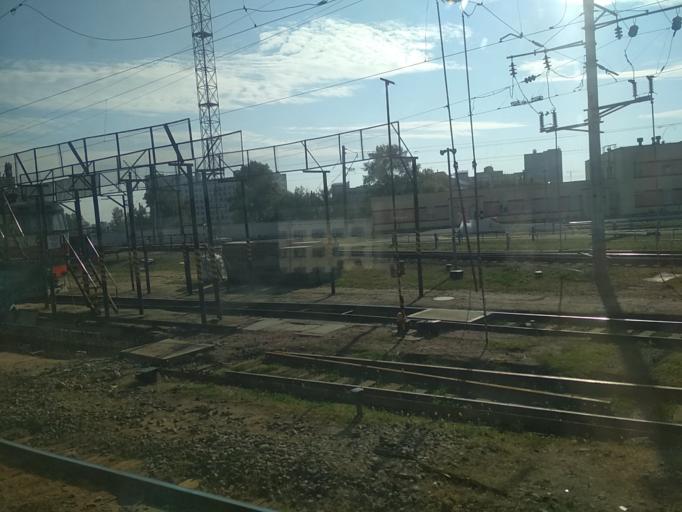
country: BY
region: Minsk
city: Minsk
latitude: 53.8894
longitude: 27.5569
